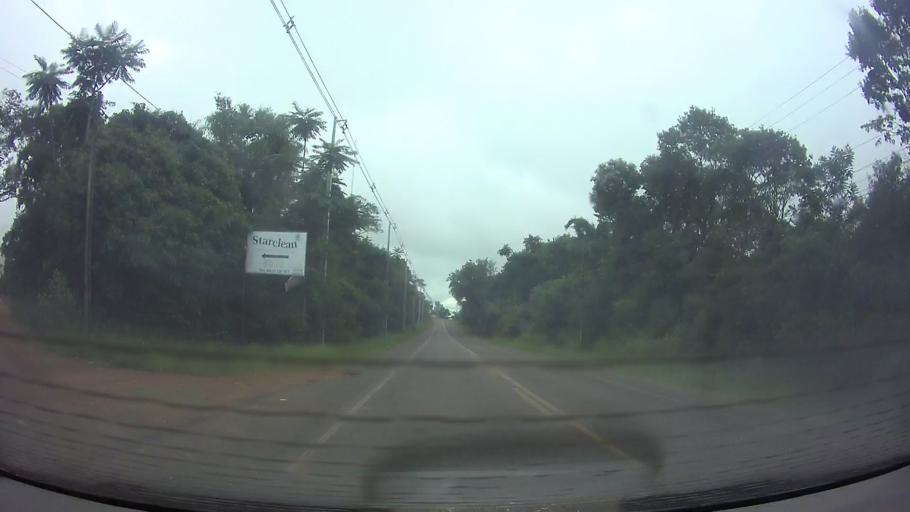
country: PY
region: Cordillera
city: Altos
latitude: -25.2780
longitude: -57.2612
